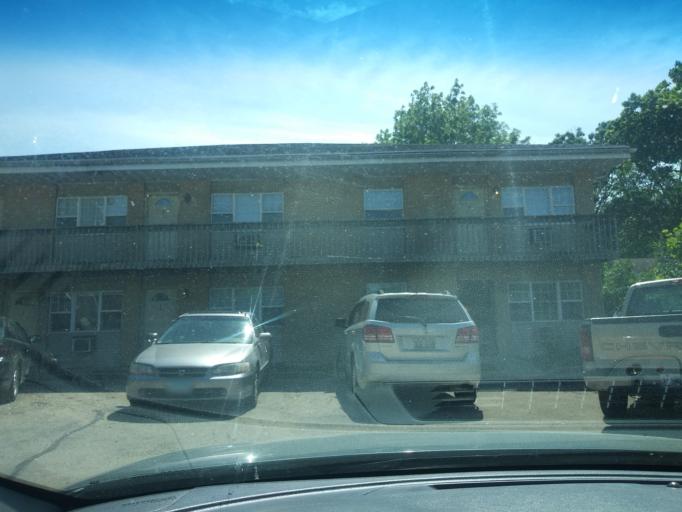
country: US
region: Illinois
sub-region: Ogle County
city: Rochelle
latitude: 41.9174
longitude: -89.0637
